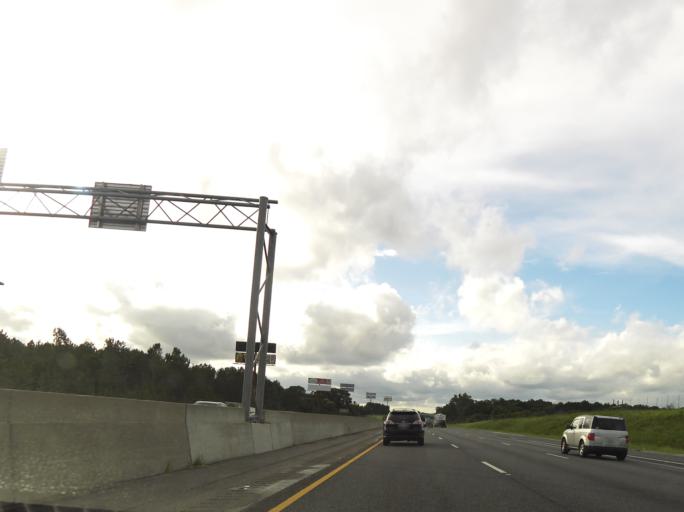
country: US
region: Georgia
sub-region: Turner County
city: Ashburn
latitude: 31.6836
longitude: -83.6221
